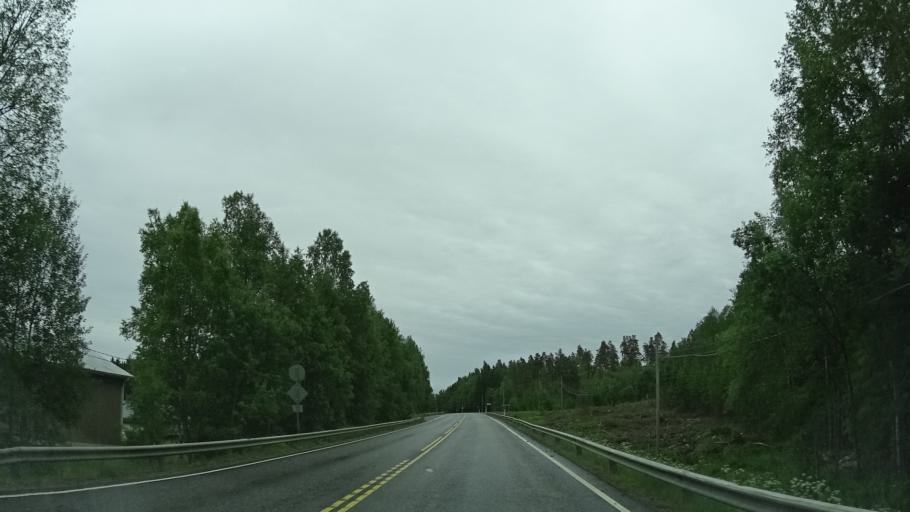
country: FI
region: Varsinais-Suomi
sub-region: Salo
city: Pernioe
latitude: 60.0968
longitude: 23.2201
